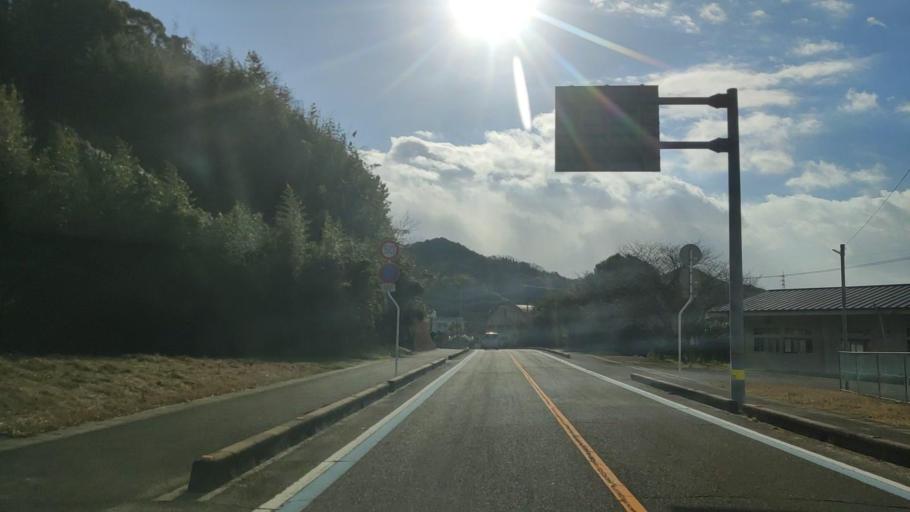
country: JP
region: Hiroshima
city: Innoshima
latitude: 34.2196
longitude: 133.0682
